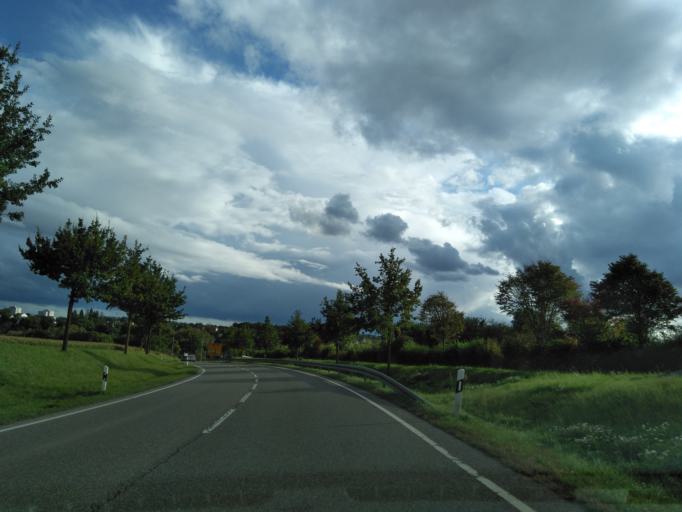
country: DE
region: Baden-Wuerttemberg
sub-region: Regierungsbezirk Stuttgart
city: Bietigheim-Bissingen
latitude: 48.9513
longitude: 9.1154
